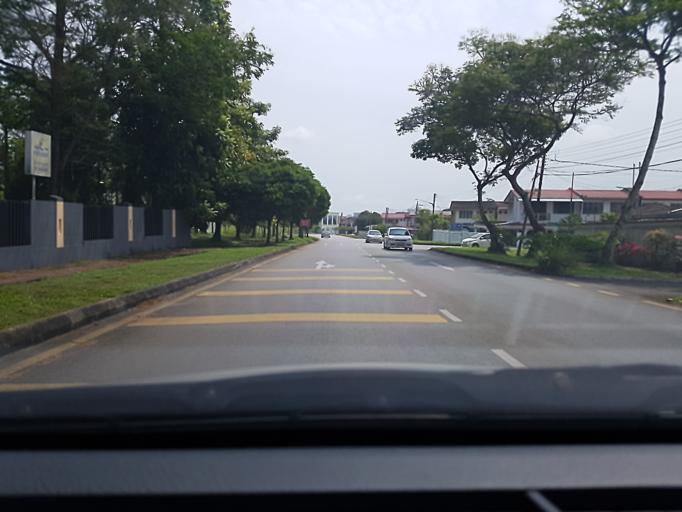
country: MY
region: Sarawak
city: Kuching
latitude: 1.5110
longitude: 110.3624
